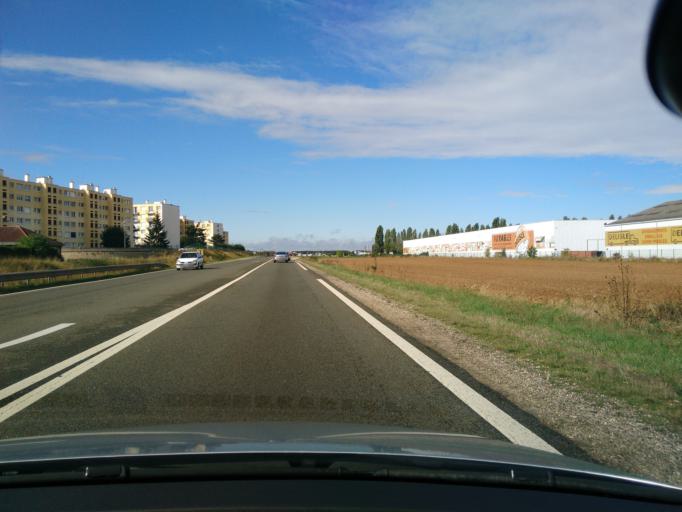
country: FR
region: Centre
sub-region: Departement d'Eure-et-Loir
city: Dreux
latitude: 48.7461
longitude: 1.3620
